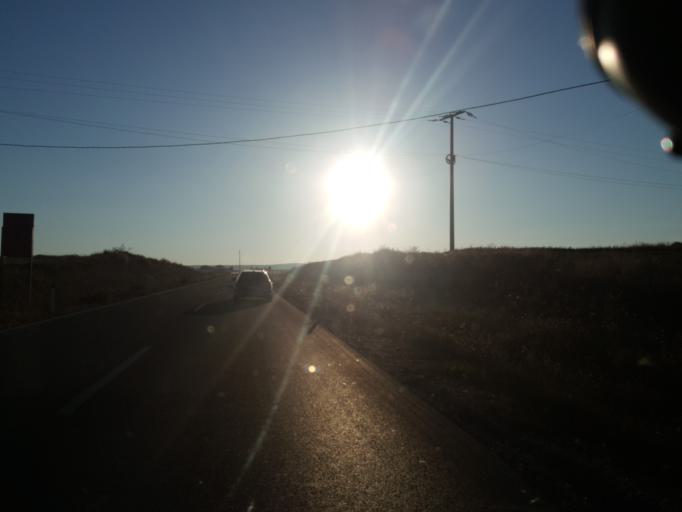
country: XK
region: Prizren
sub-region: Komuna e Malisheves
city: Llazice
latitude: 42.5758
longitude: 20.7110
